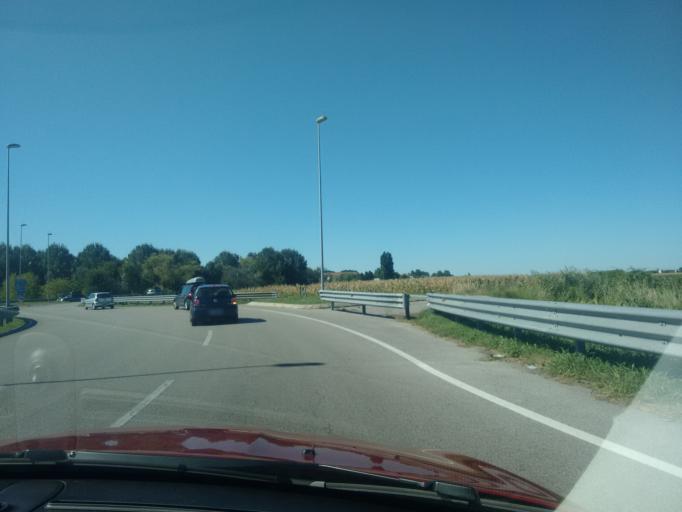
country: IT
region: Veneto
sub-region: Provincia di Venezia
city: Caorle
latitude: 45.5831
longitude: 12.8262
